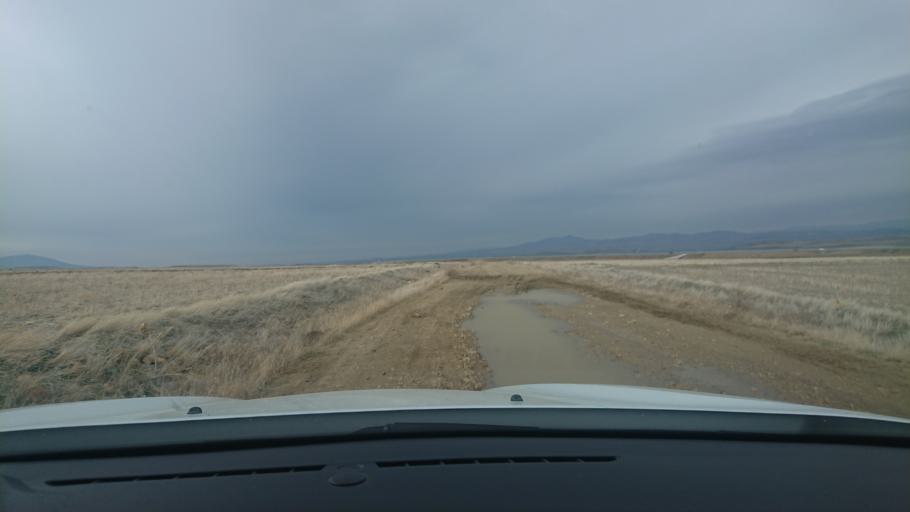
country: TR
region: Aksaray
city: Sariyahsi
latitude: 38.9817
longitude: 33.8779
